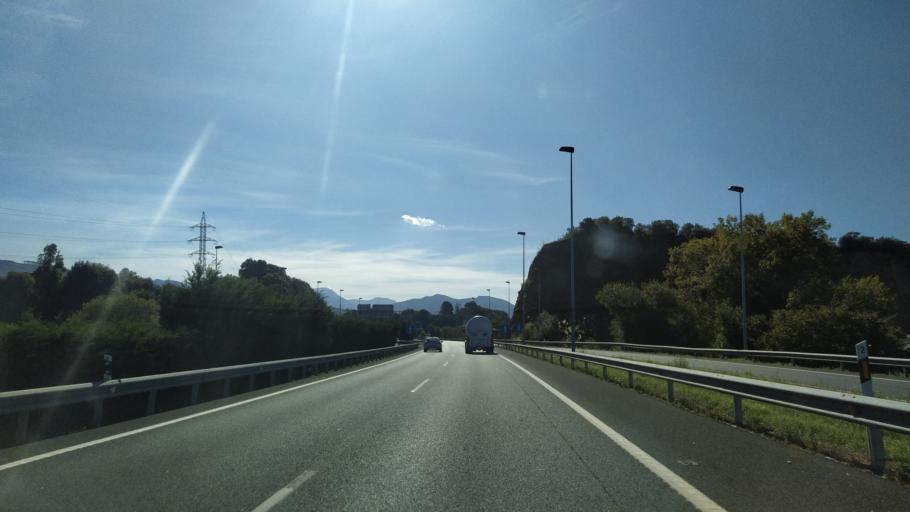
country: ES
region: Cantabria
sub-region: Provincia de Cantabria
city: Colindres
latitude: 43.3997
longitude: -3.4384
